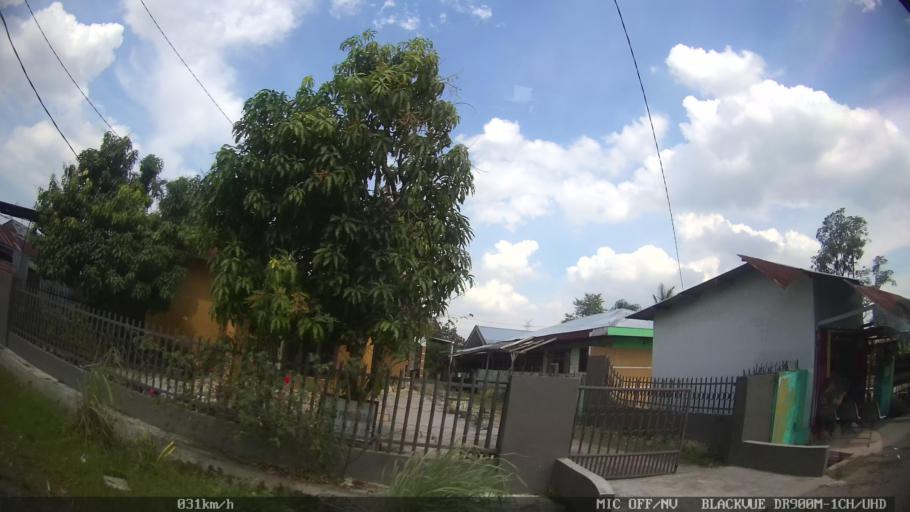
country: ID
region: North Sumatra
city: Binjai
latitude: 3.6237
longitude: 98.5009
